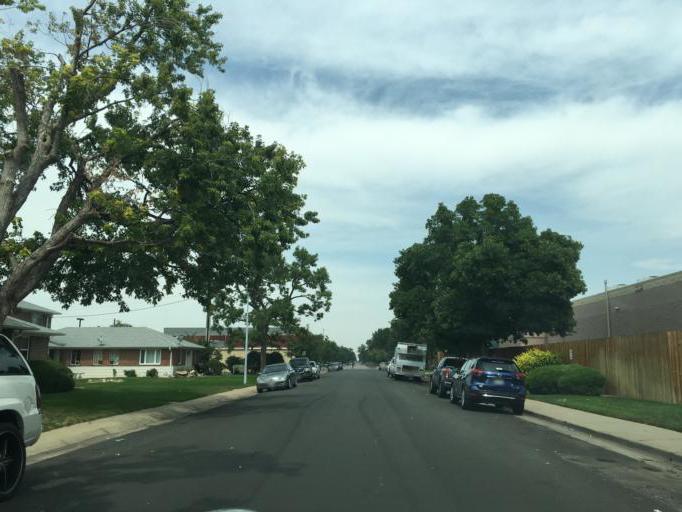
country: US
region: Colorado
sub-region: Adams County
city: Aurora
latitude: 39.7387
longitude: -104.8682
